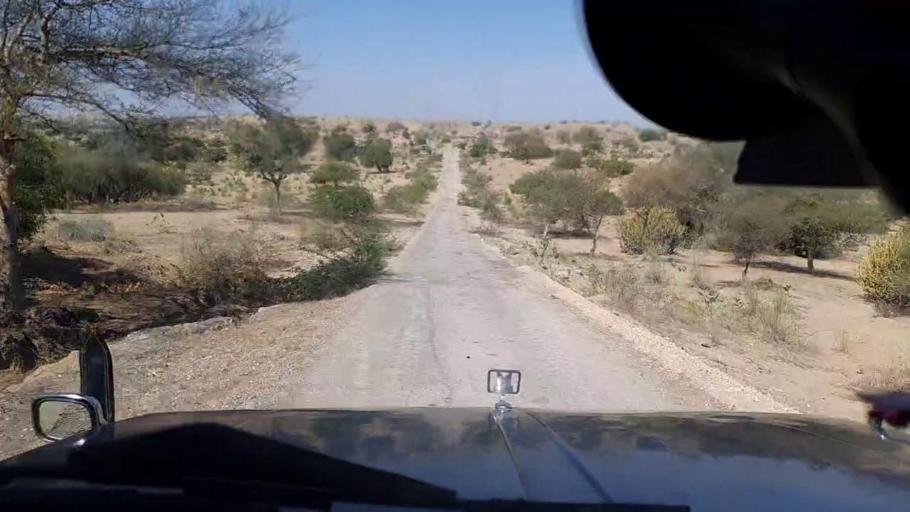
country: PK
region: Sindh
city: Mithi
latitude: 24.6118
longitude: 69.7002
